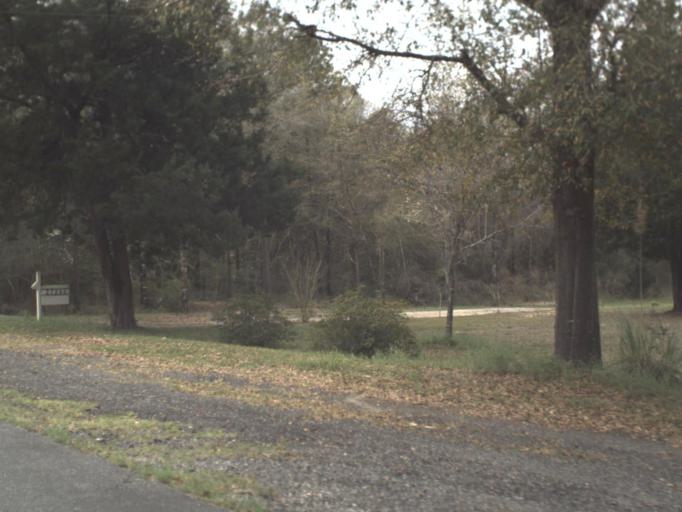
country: US
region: Florida
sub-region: Calhoun County
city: Blountstown
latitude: 30.5630
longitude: -85.1837
